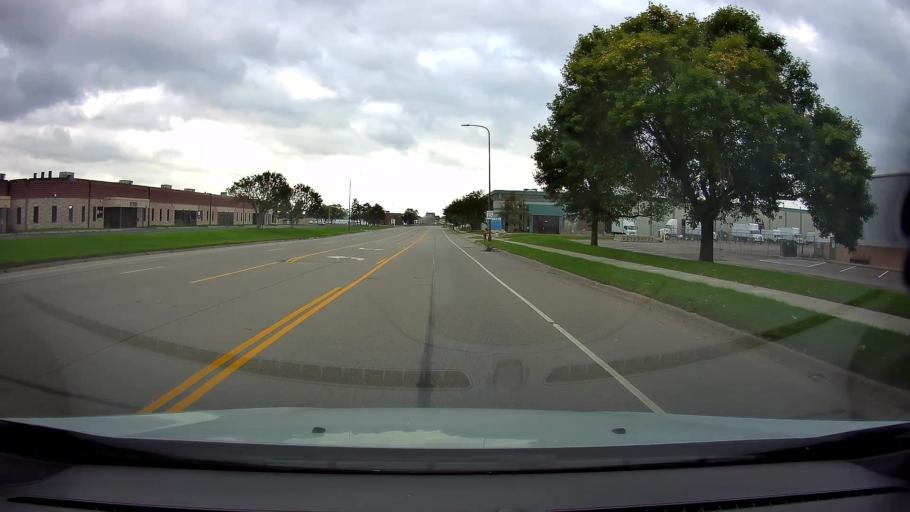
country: US
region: Minnesota
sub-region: Ramsey County
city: Falcon Heights
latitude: 44.9652
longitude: -93.1858
